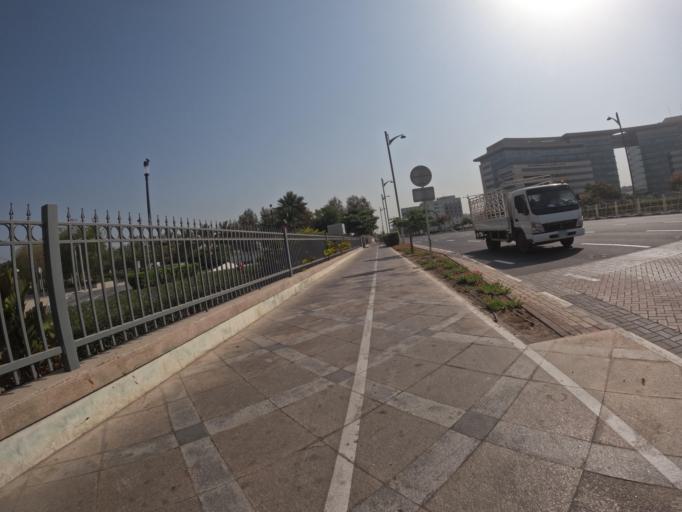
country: AE
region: Ash Shariqah
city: Sharjah
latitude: 25.2414
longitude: 55.2695
